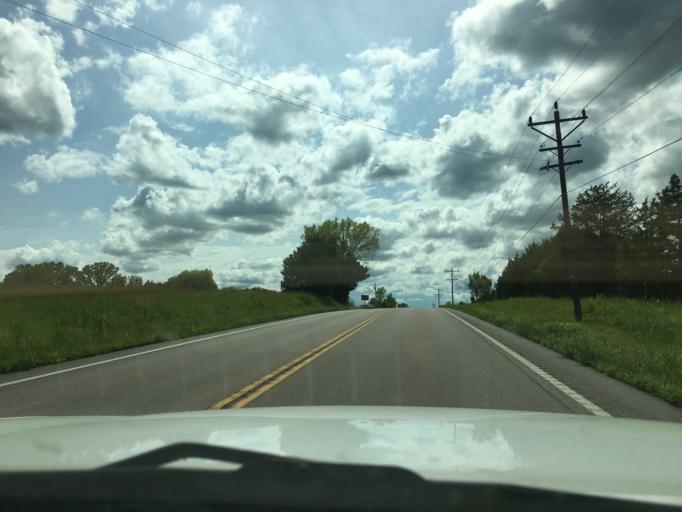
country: US
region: Missouri
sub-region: Franklin County
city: Gerald
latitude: 38.3874
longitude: -91.3881
